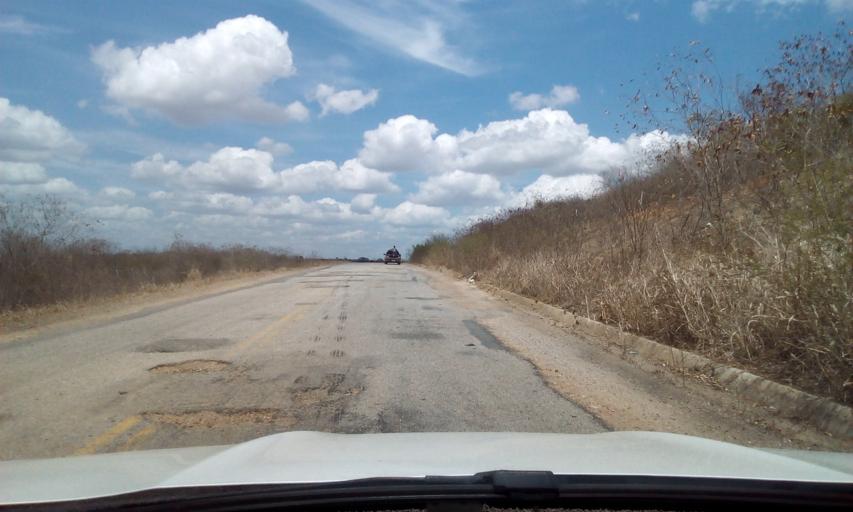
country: BR
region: Paraiba
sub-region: Gurinhem
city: Gurinhem
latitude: -7.0897
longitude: -35.4490
